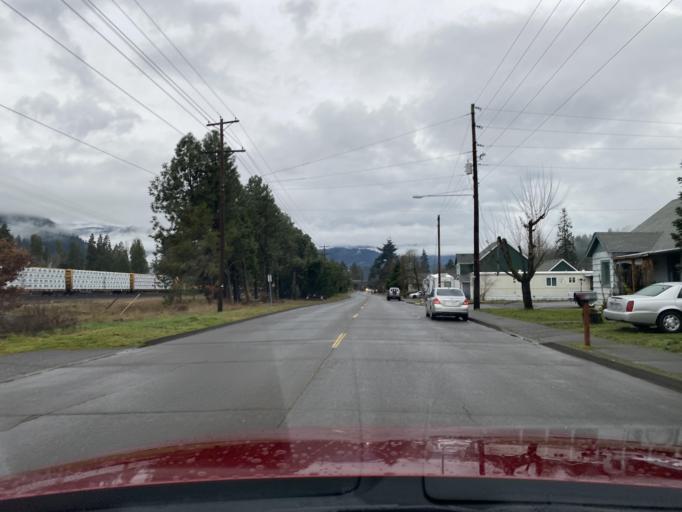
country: US
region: Oregon
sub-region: Lane County
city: Oakridge
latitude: 43.7470
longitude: -122.4617
